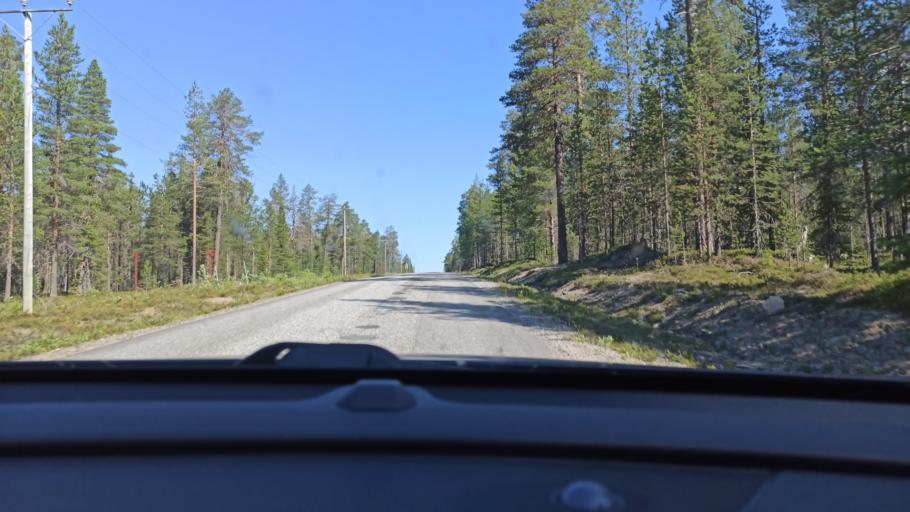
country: FI
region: Lapland
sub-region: Tunturi-Lappi
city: Kolari
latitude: 67.6378
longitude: 24.1565
